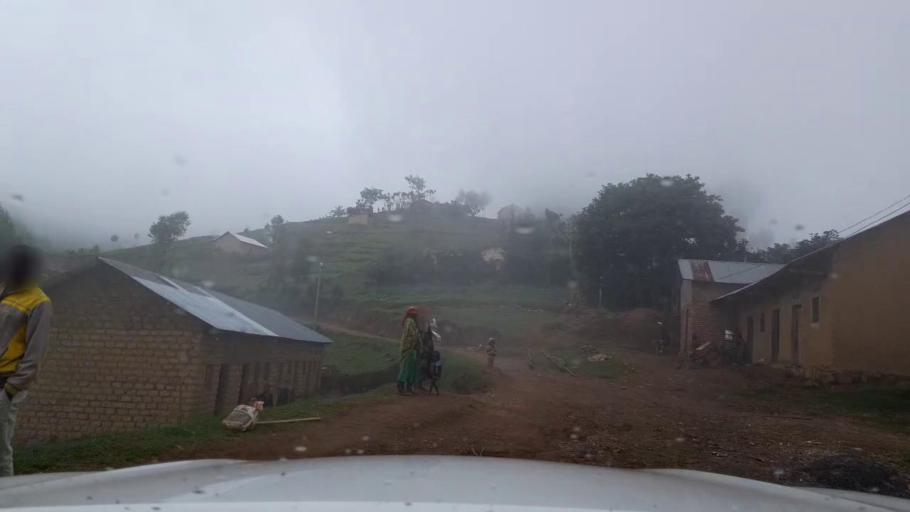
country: RW
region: Northern Province
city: Musanze
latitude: -1.5972
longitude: 29.7926
